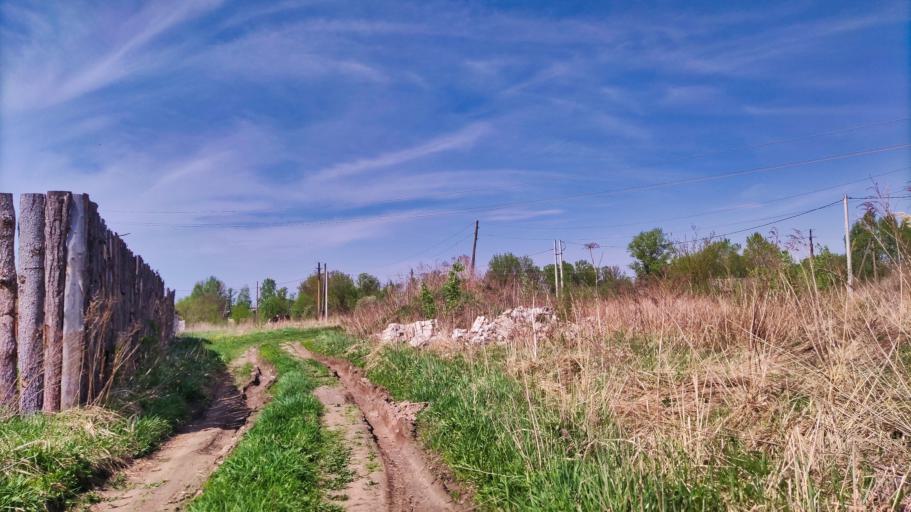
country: RU
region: Tverskaya
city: Rzhev
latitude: 56.2361
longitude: 34.3262
